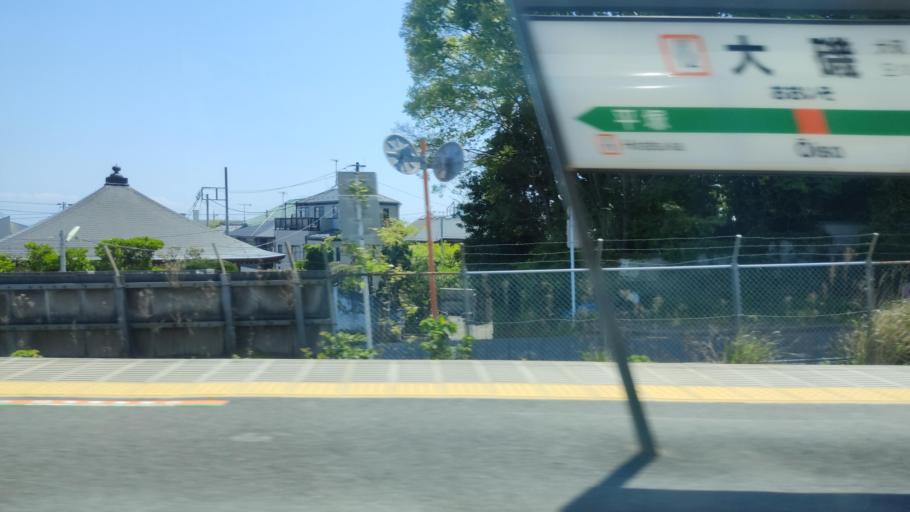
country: JP
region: Kanagawa
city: Oiso
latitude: 35.3121
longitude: 139.3145
